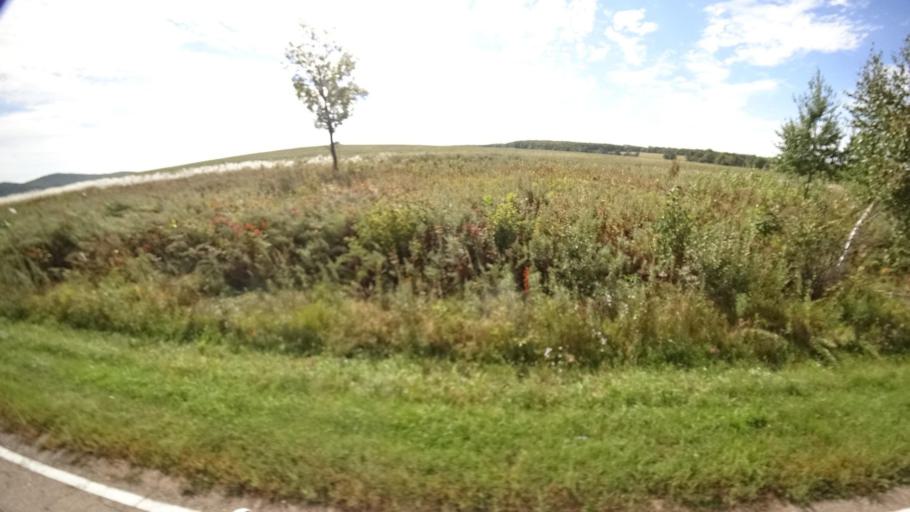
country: RU
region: Primorskiy
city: Yakovlevka
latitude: 44.4172
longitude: 133.5825
